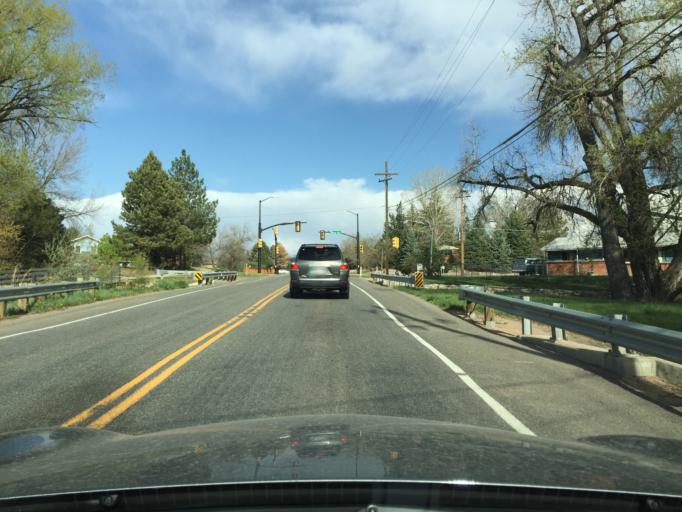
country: US
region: Colorado
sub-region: Boulder County
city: Niwot
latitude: 40.1016
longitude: -105.1501
